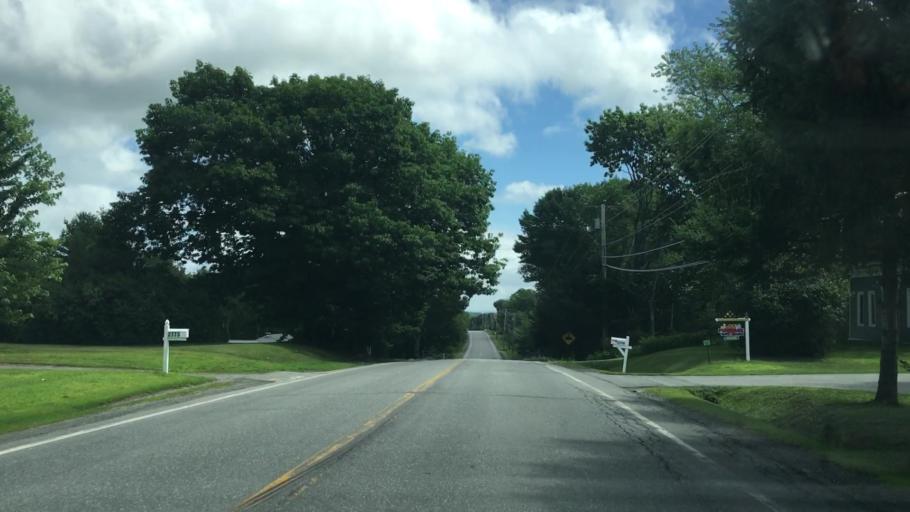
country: US
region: Maine
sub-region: Penobscot County
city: Hermon
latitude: 44.8071
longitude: -68.9365
